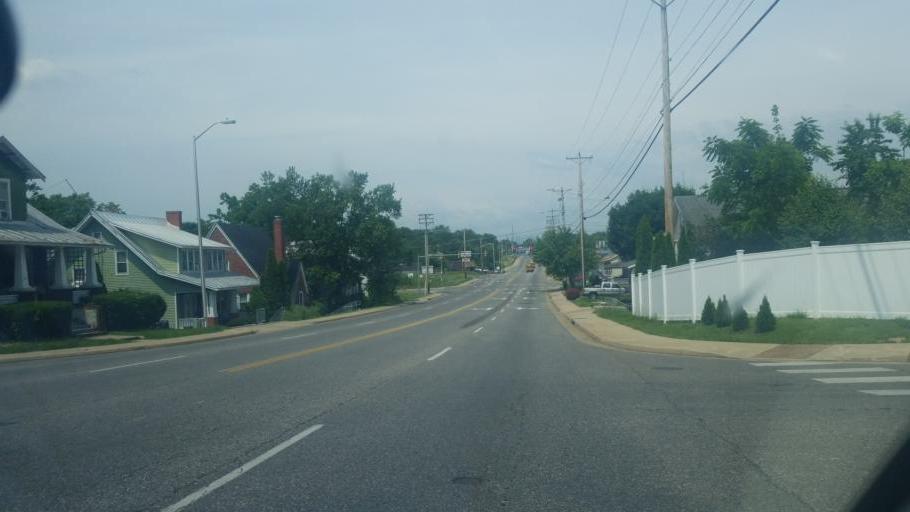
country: US
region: Virginia
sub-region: City of Harrisonburg
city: Harrisonburg
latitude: 38.4508
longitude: -78.8772
